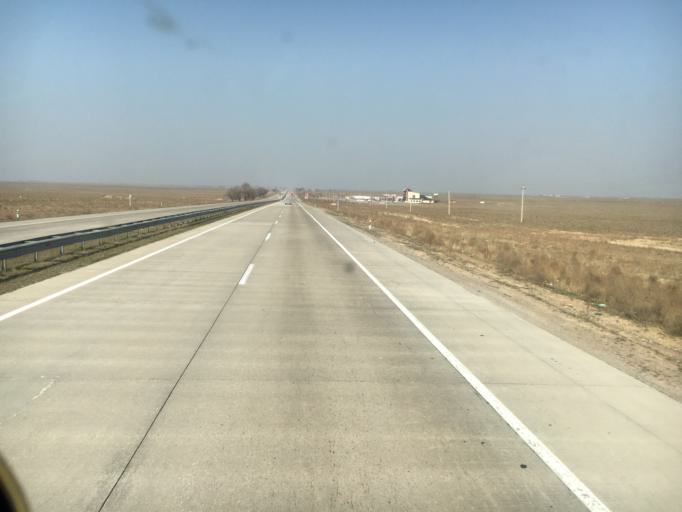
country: KZ
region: Ongtustik Qazaqstan
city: Temirlanovka
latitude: 42.8376
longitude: 69.1127
